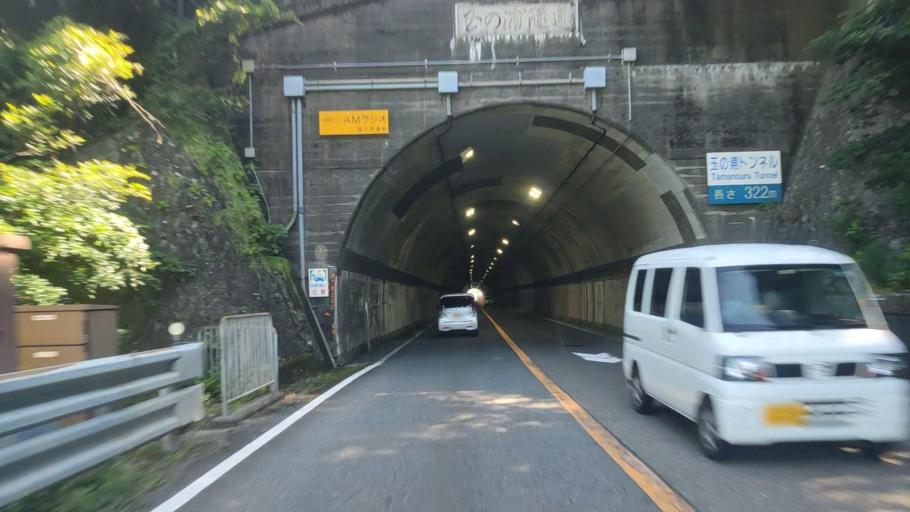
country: JP
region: Wakayama
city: Shingu
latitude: 33.5760
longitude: 135.9186
